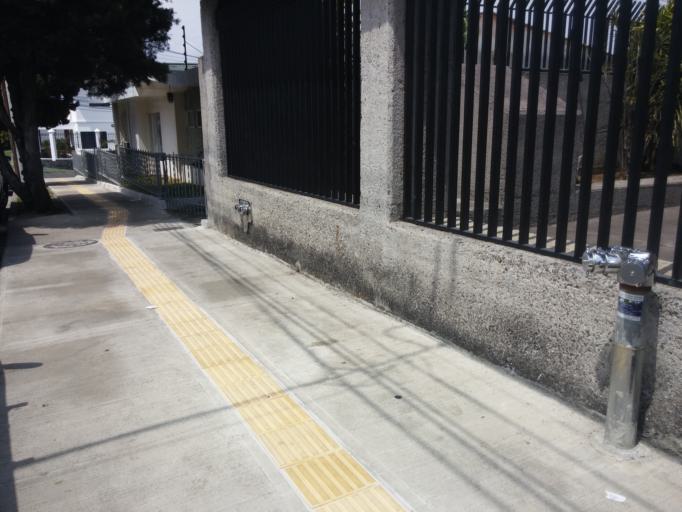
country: CR
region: Heredia
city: San Francisco
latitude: 9.9992
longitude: -84.1241
